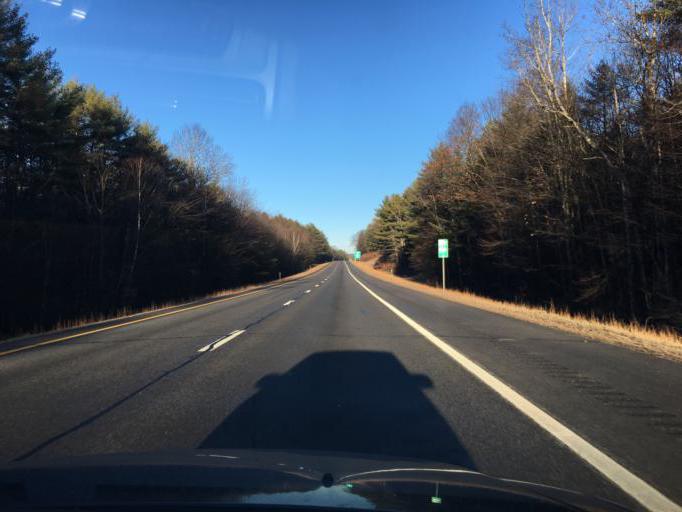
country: US
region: New Hampshire
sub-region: Belknap County
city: Sanbornton
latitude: 43.4967
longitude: -71.6047
